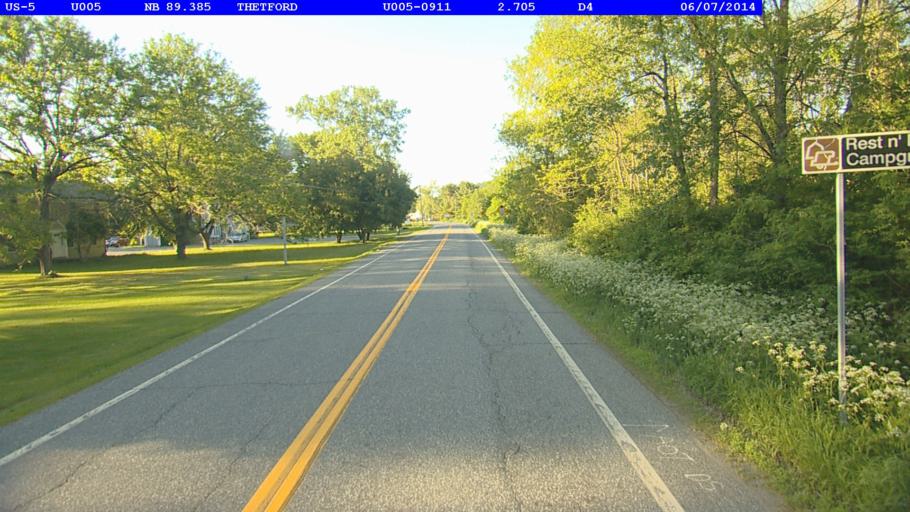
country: US
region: New Hampshire
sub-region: Grafton County
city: Lyme
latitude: 43.8076
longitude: -72.1899
